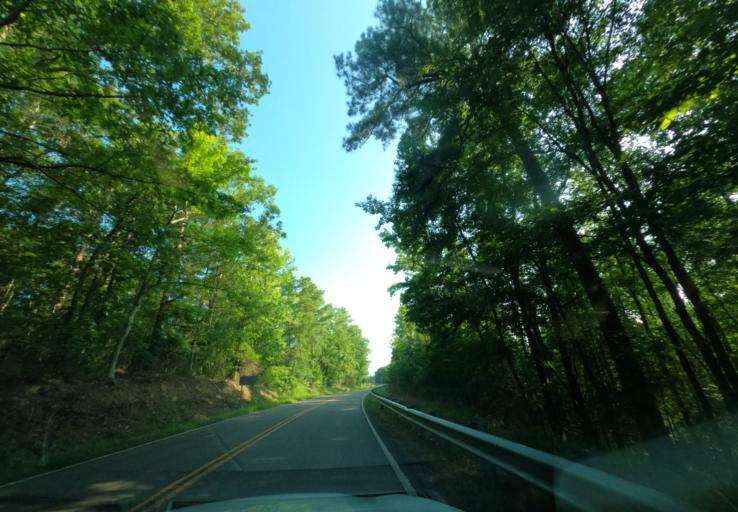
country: US
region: South Carolina
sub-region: Edgefield County
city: Murphys Estates
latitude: 33.6258
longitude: -81.9729
